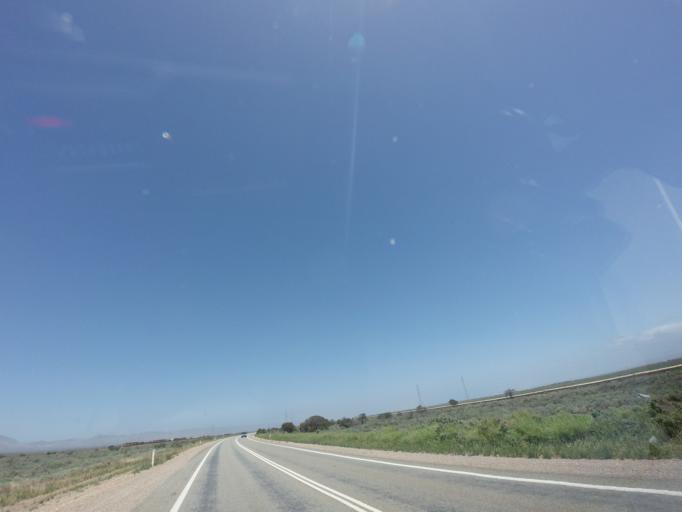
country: AU
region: South Australia
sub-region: Port Augusta
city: Port Augusta
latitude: -32.5420
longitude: 137.8554
